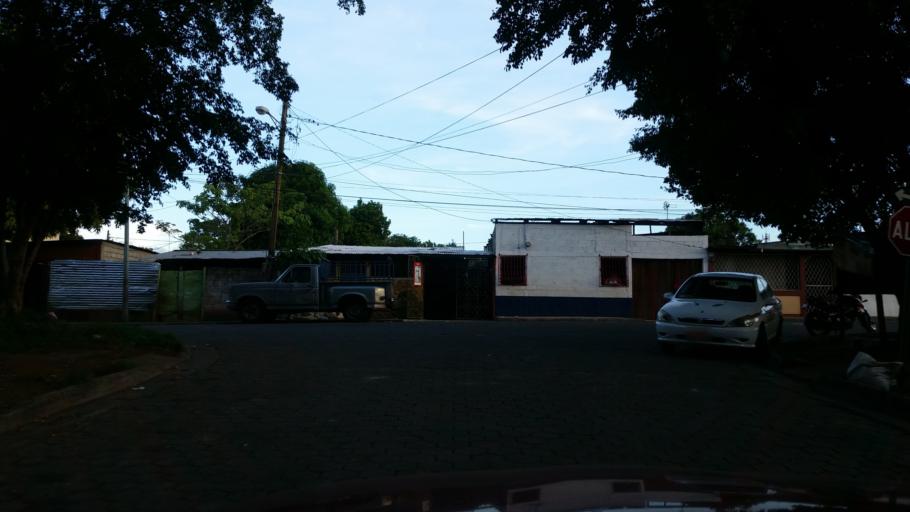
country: NI
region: Managua
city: Managua
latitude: 12.1329
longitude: -86.2874
